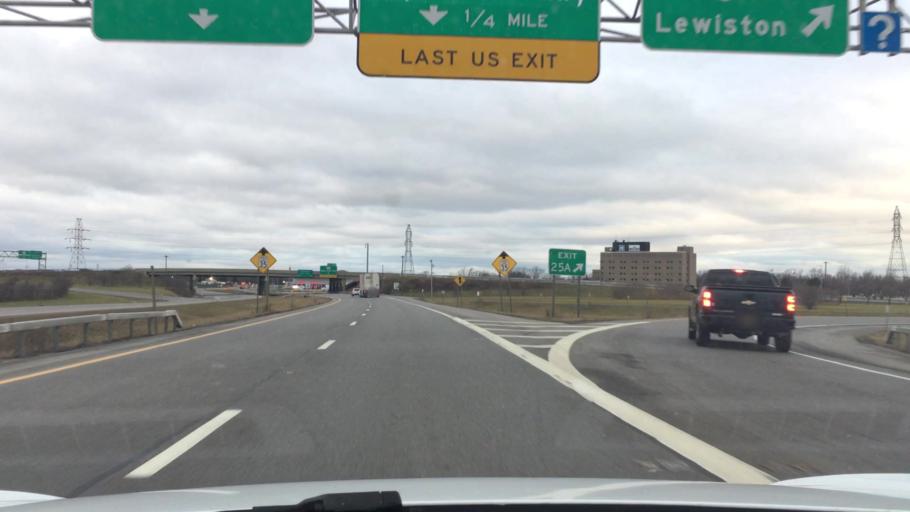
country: US
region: New York
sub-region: Niagara County
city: Lewiston
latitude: 43.1502
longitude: -79.0279
